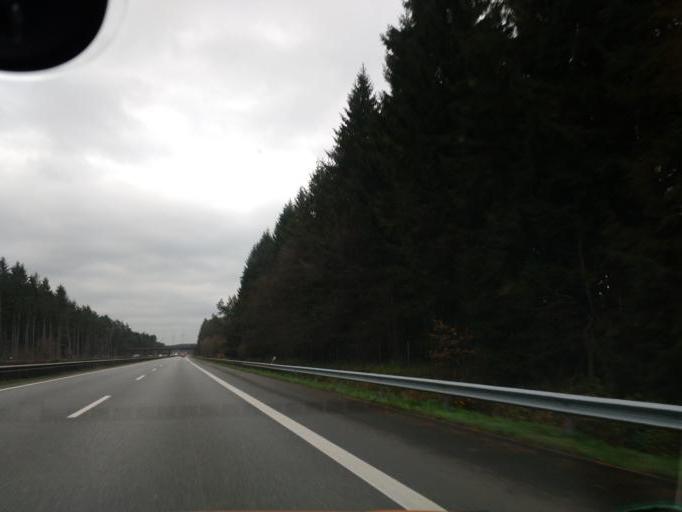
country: DE
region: Lower Saxony
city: Hauslingen
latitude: 52.8977
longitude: 9.4219
